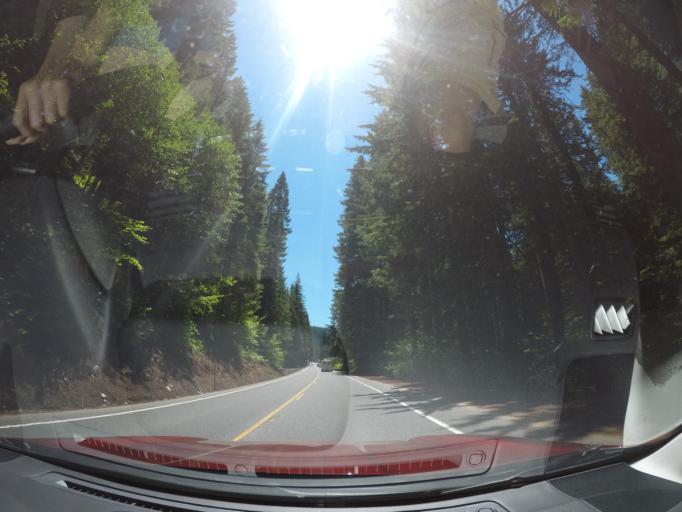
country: US
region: Oregon
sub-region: Linn County
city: Mill City
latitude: 44.5616
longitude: -121.9996
